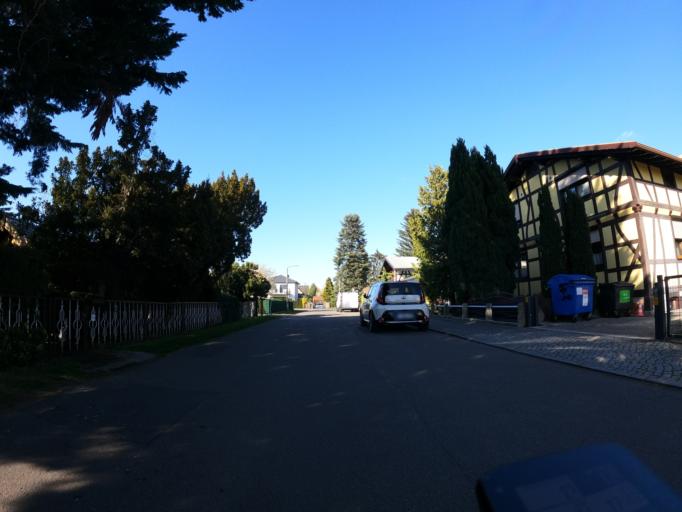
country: DE
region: Berlin
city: Marzahn
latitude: 52.5411
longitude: 13.5541
